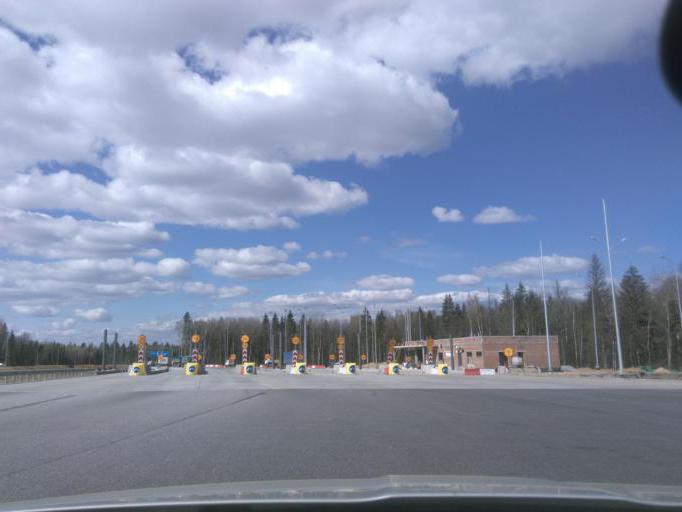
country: RU
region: Moskovskaya
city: Peshki
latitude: 56.1403
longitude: 37.0721
